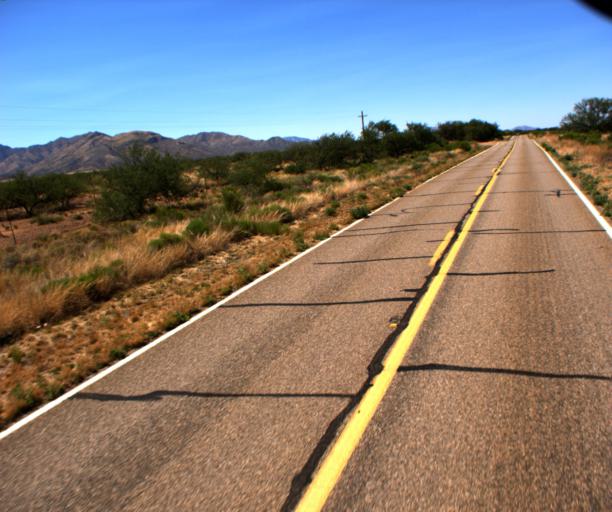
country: US
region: Arizona
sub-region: Pima County
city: Three Points
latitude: 31.7233
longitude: -111.4879
